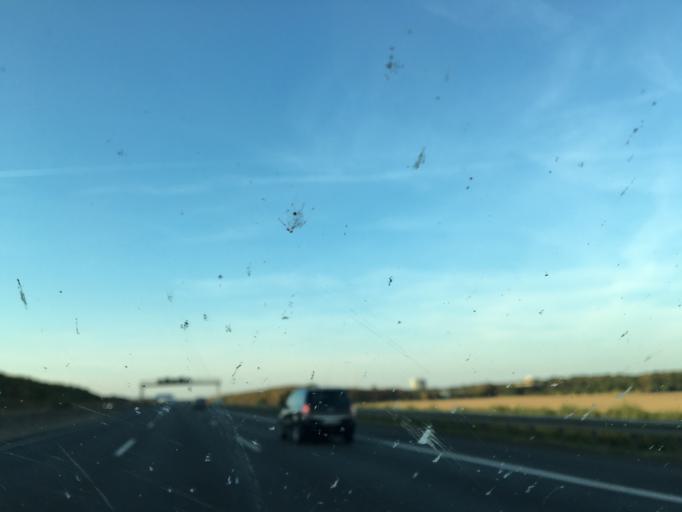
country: DE
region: North Rhine-Westphalia
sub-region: Regierungsbezirk Koln
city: Mengenich
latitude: 50.9633
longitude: 6.8508
